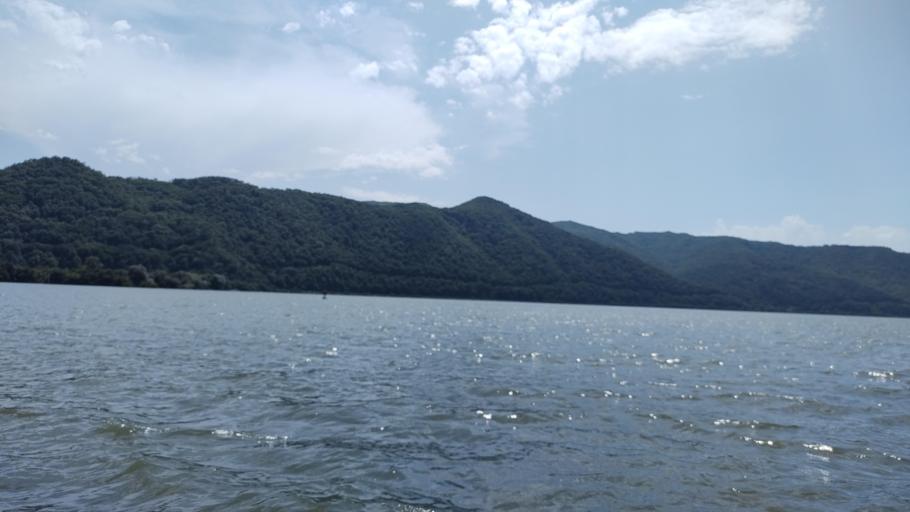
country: RO
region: Caras-Severin
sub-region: Comuna Berzasca
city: Liubcova
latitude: 44.6537
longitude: 21.8393
